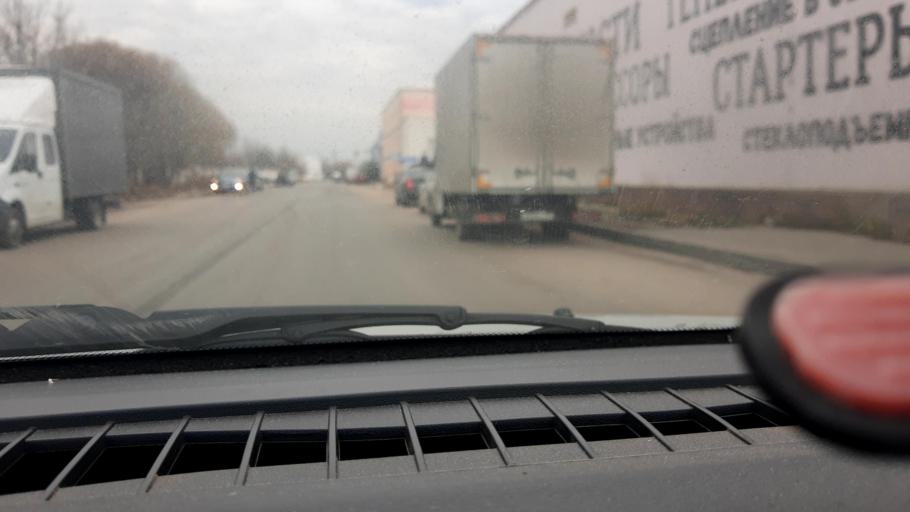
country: RU
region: Nizjnij Novgorod
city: Nizhniy Novgorod
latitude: 56.2939
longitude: 43.8786
